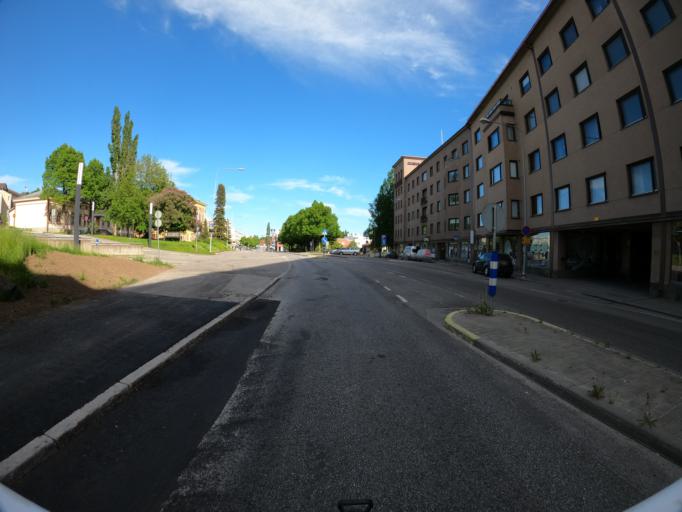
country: FI
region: Southern Savonia
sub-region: Savonlinna
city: Savonlinna
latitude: 61.8673
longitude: 28.8897
